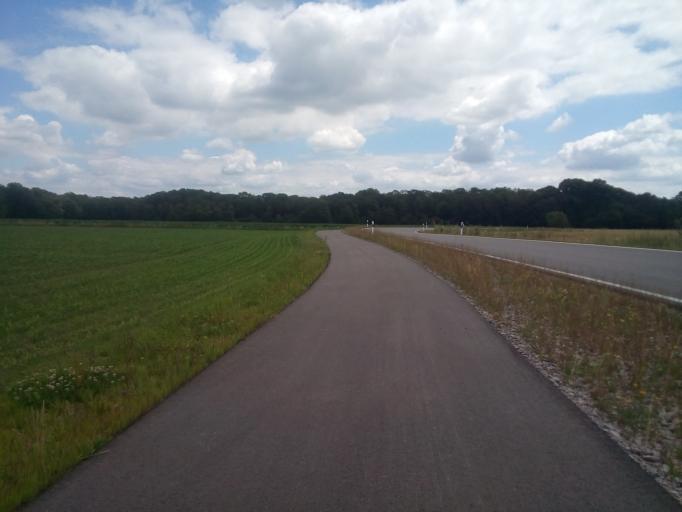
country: DE
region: Baden-Wuerttemberg
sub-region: Freiburg Region
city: Rheinau
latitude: 48.6400
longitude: 7.9419
